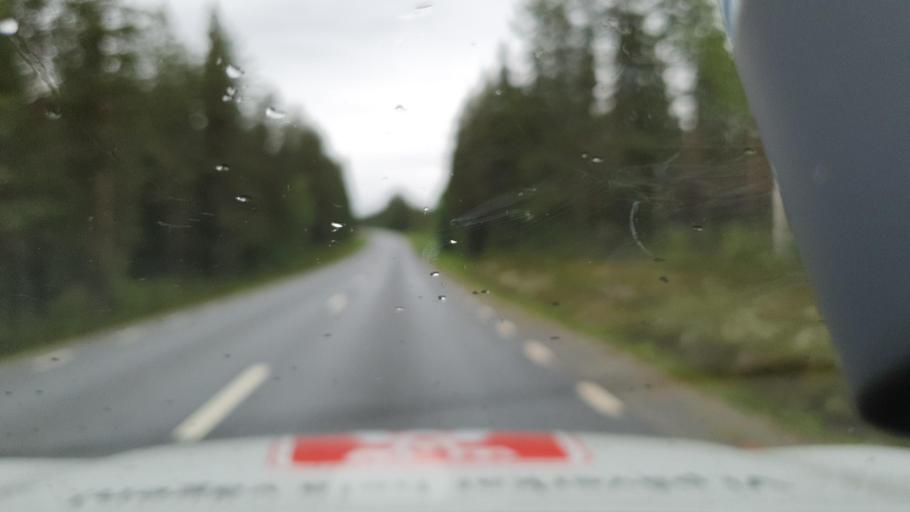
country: SE
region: Vaesterbotten
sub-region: Bjurholms Kommun
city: Bjurholm
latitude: 63.9810
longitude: 18.8103
